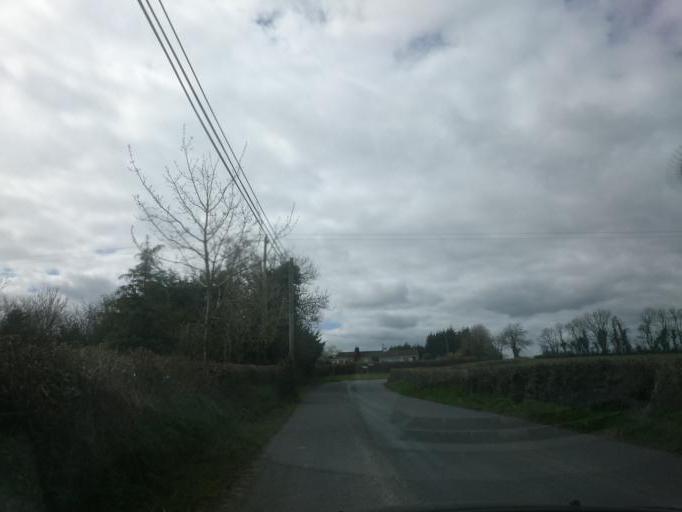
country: IE
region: Leinster
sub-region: Kilkenny
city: Kilkenny
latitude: 52.6643
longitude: -7.3295
